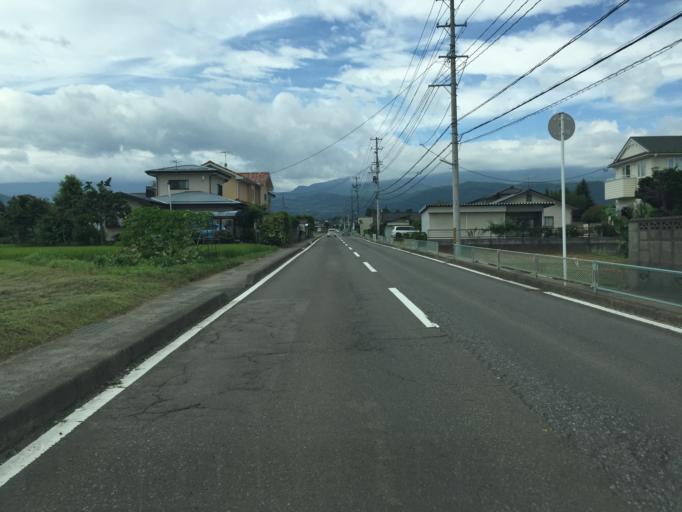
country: JP
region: Fukushima
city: Fukushima-shi
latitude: 37.7325
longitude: 140.3941
